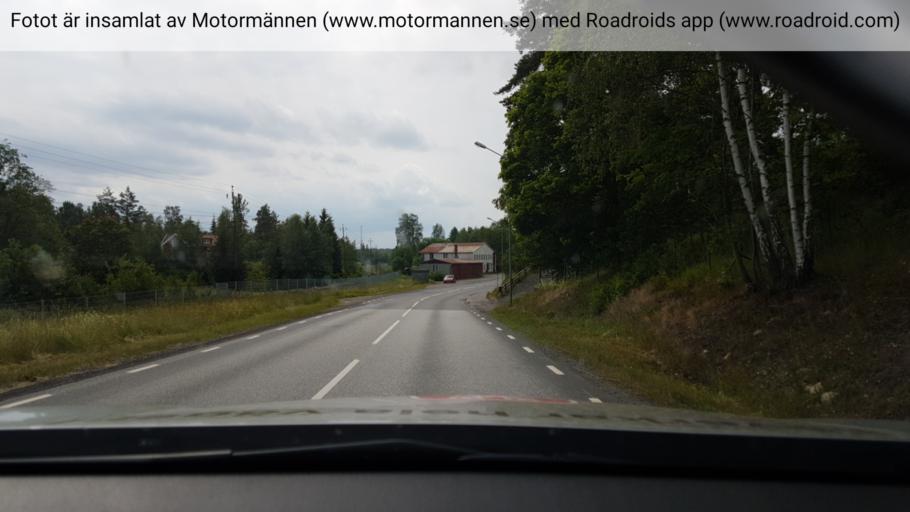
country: SE
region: Joenkoeping
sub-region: Mullsjo Kommun
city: Mullsjoe
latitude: 57.9213
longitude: 13.9016
